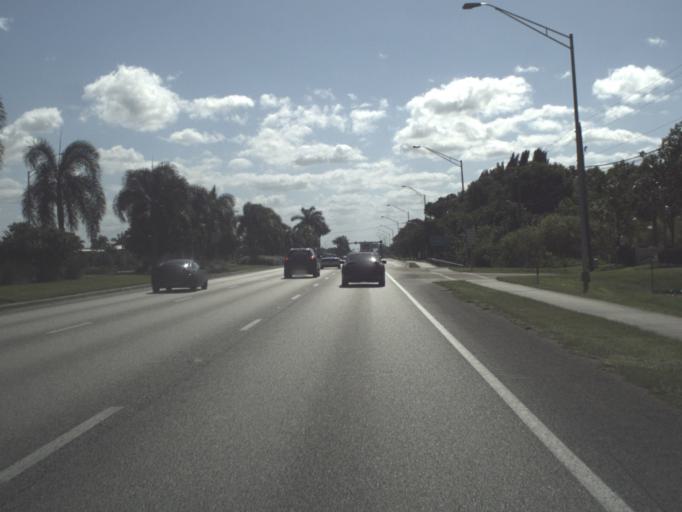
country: US
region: Florida
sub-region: Collier County
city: Lely Resort
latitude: 26.0676
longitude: -81.7062
